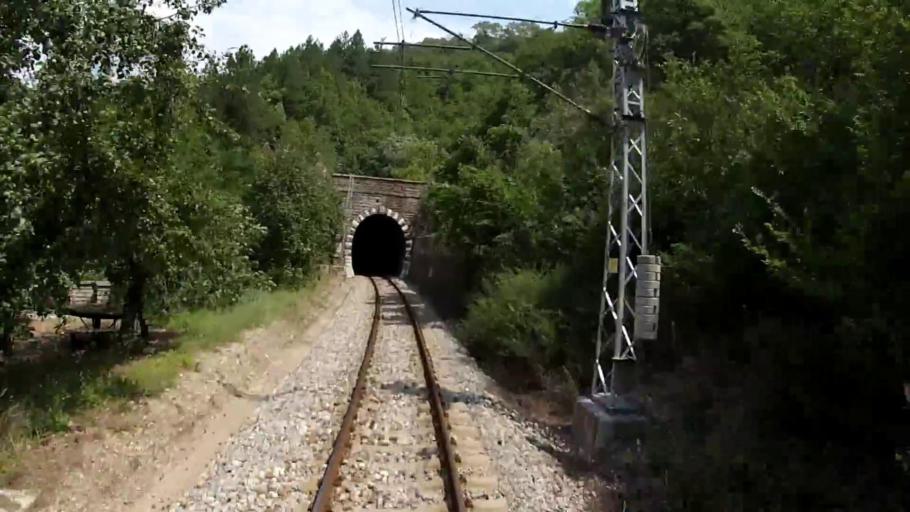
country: BG
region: Blagoevgrad
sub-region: Obshtina Kresna
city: Stara Kresna
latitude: 41.7797
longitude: 23.1554
